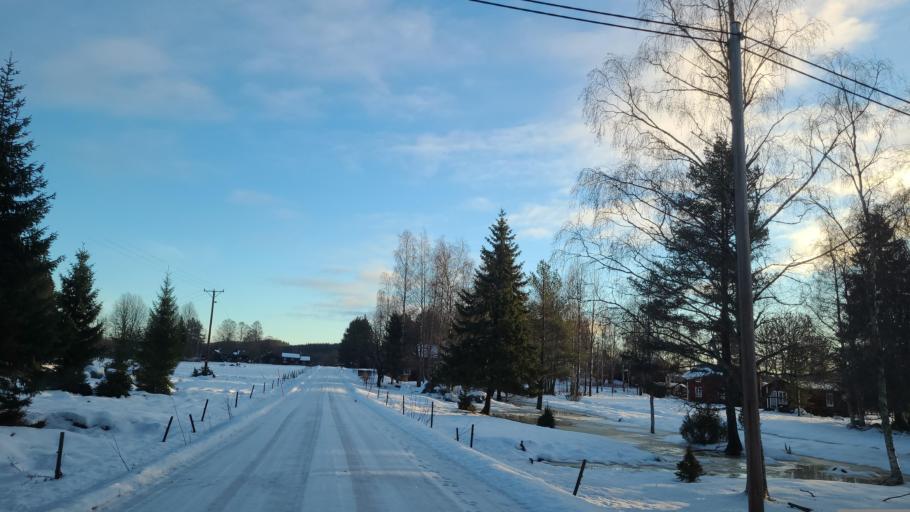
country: SE
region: Gaevleborg
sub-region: Bollnas Kommun
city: Kilafors
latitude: 61.3985
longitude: 16.6661
